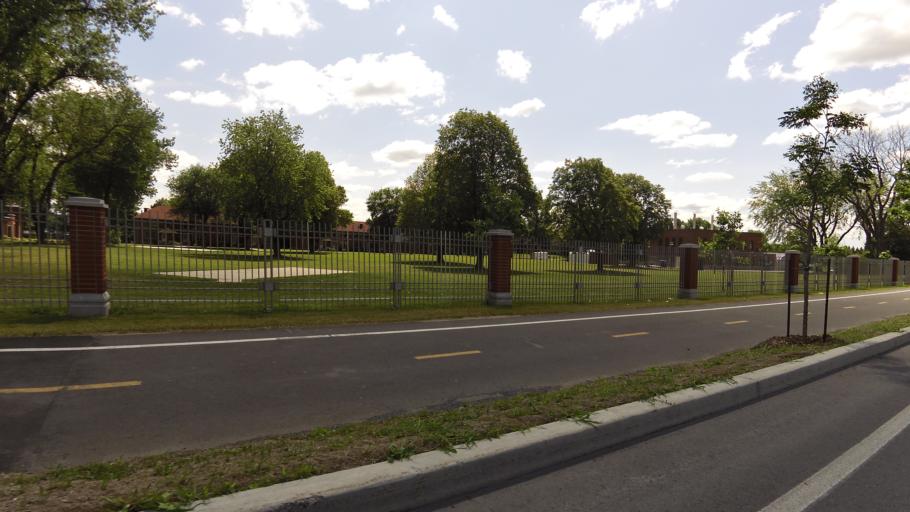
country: CA
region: Quebec
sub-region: Monteregie
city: Saint-Jean-sur-Richelieu
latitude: 45.3012
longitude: -73.2534
